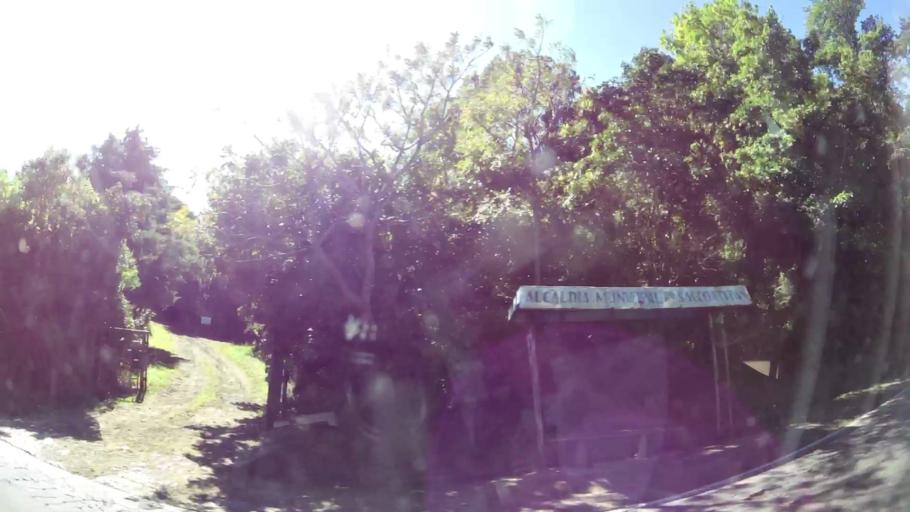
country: SV
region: Sonsonate
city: Juayua
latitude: 13.8532
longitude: -89.7699
